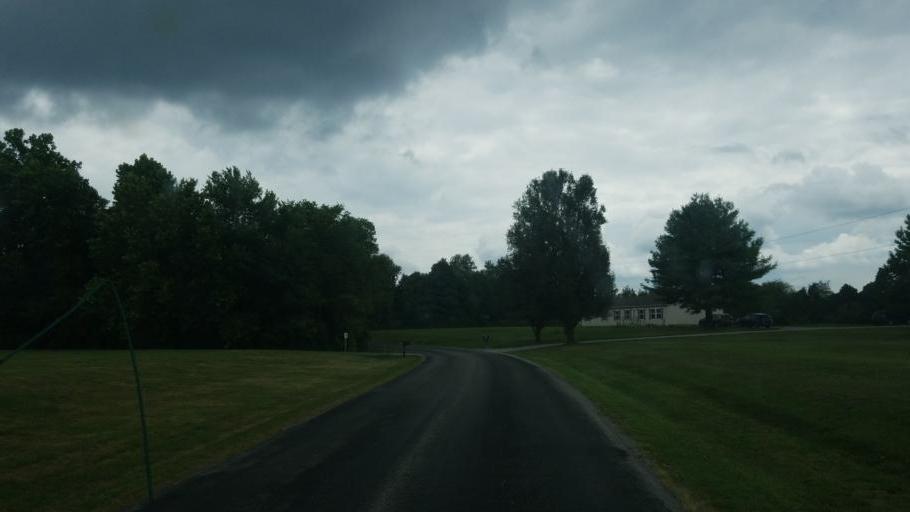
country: US
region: Illinois
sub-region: Jackson County
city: Murphysboro
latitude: 37.7053
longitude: -89.3320
